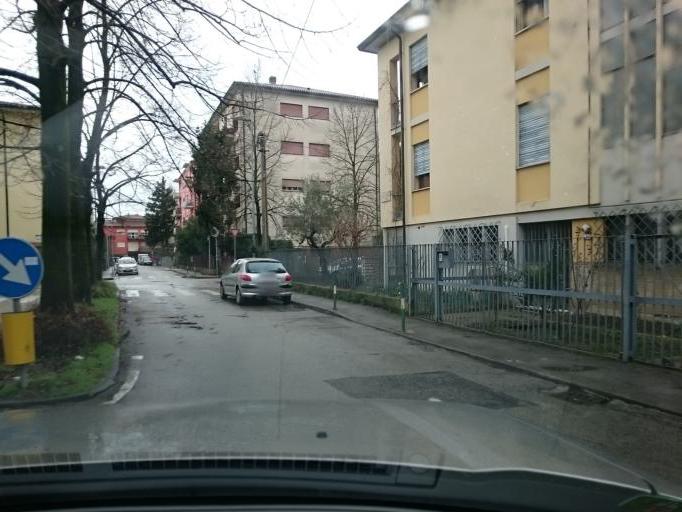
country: IT
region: Veneto
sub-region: Provincia di Padova
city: Padova
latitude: 45.4283
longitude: 11.8818
